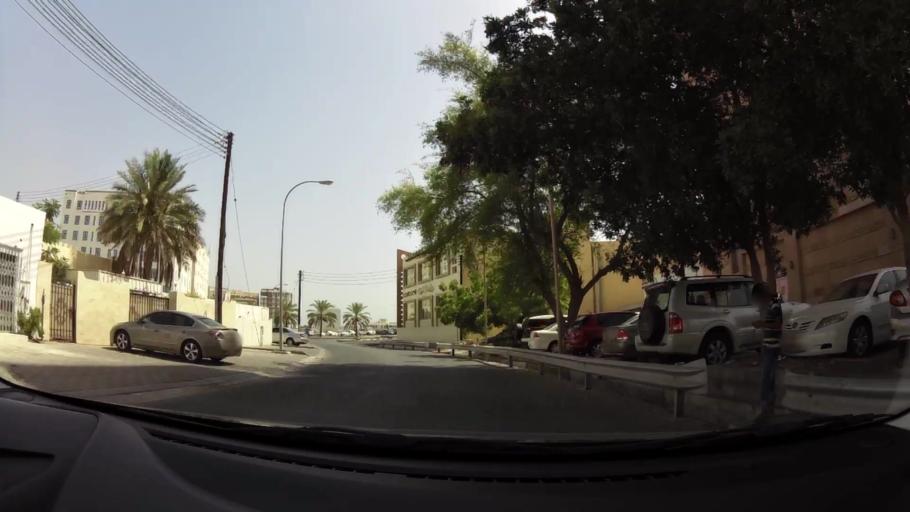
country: OM
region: Muhafazat Masqat
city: Bawshar
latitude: 23.5925
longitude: 58.4271
